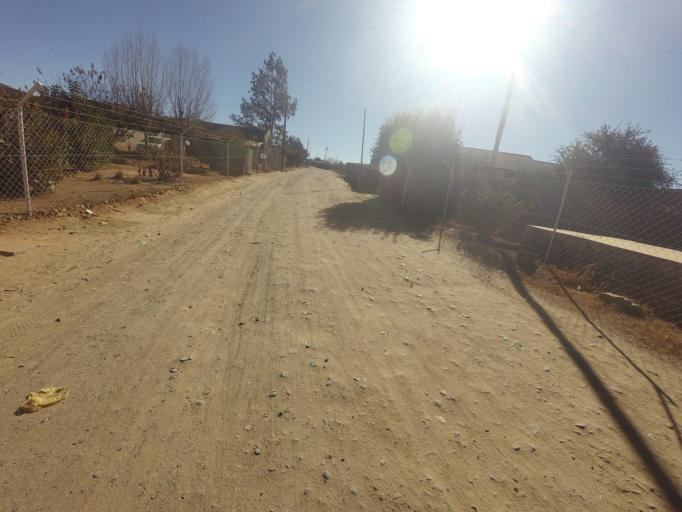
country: LS
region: Maseru
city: Maseru
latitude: -29.2972
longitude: 27.5393
